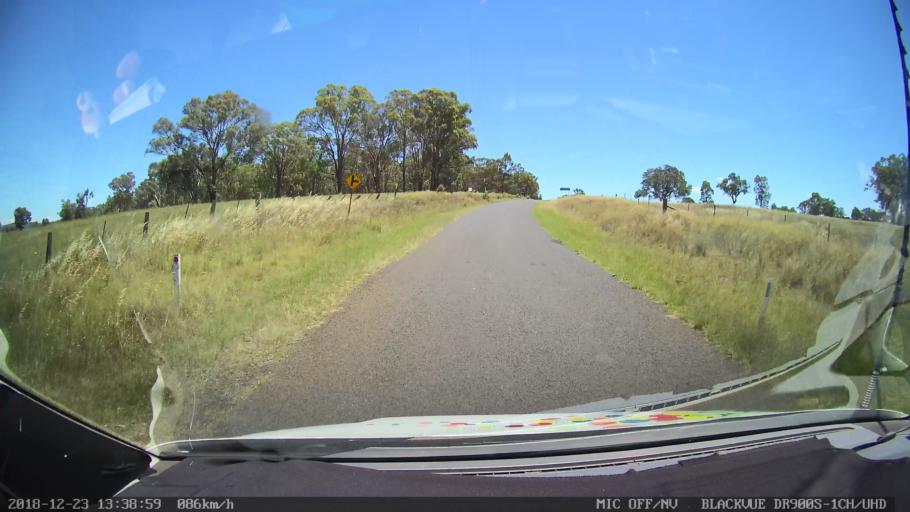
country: AU
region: New South Wales
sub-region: Armidale Dumaresq
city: Armidale
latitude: -30.4544
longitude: 151.2069
